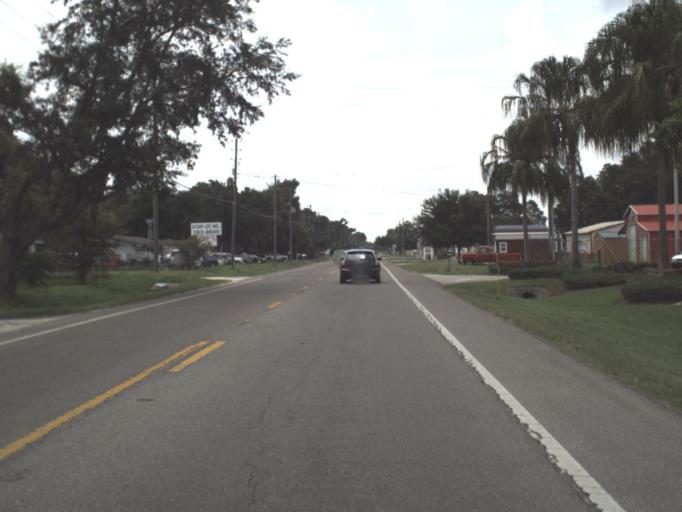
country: US
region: Florida
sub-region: Pasco County
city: Zephyrhills West
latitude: 28.2300
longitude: -82.2077
